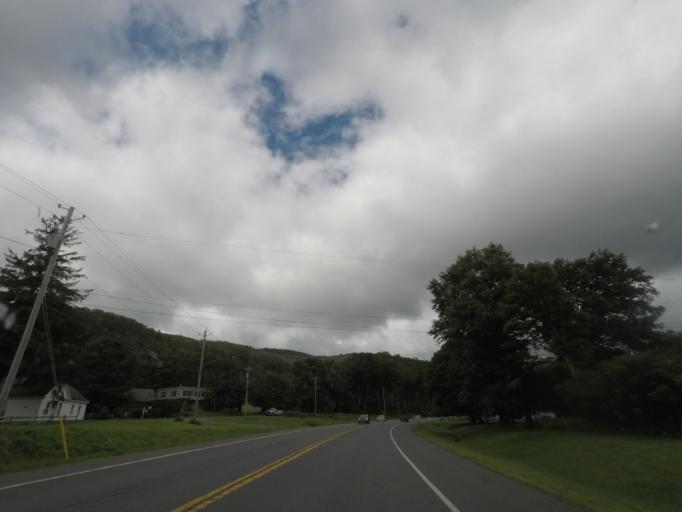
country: US
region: Massachusetts
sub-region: Berkshire County
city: Williamstown
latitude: 42.6612
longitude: -73.3692
